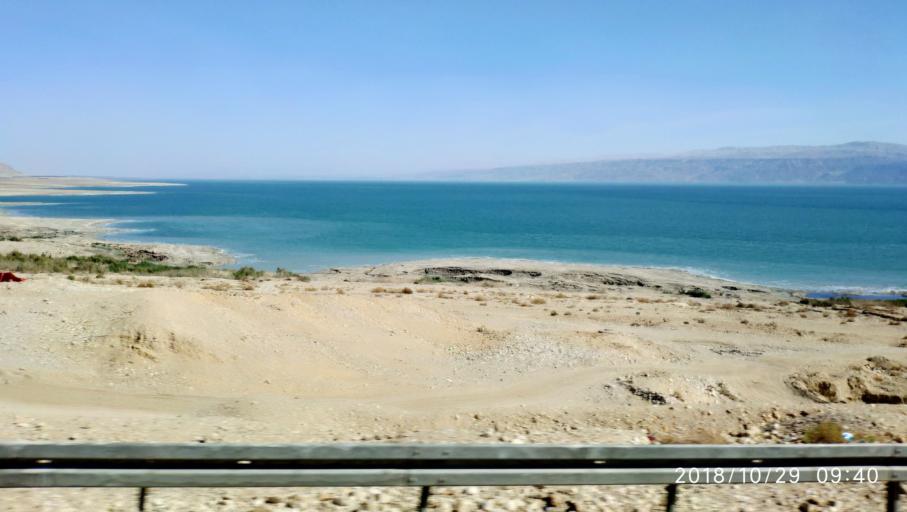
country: PS
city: `Arab ar Rashaydah
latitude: 31.5807
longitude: 35.4082
